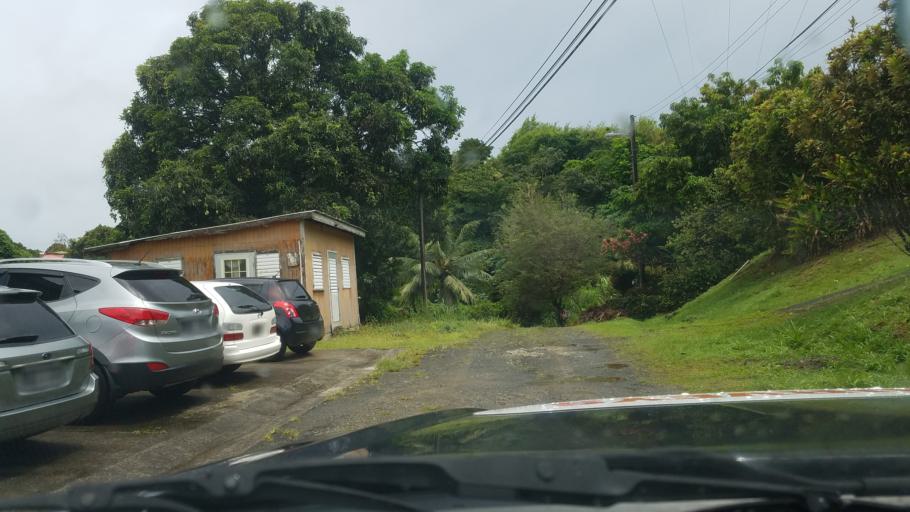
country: LC
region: Castries Quarter
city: Castries
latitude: 13.9949
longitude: -61.0009
